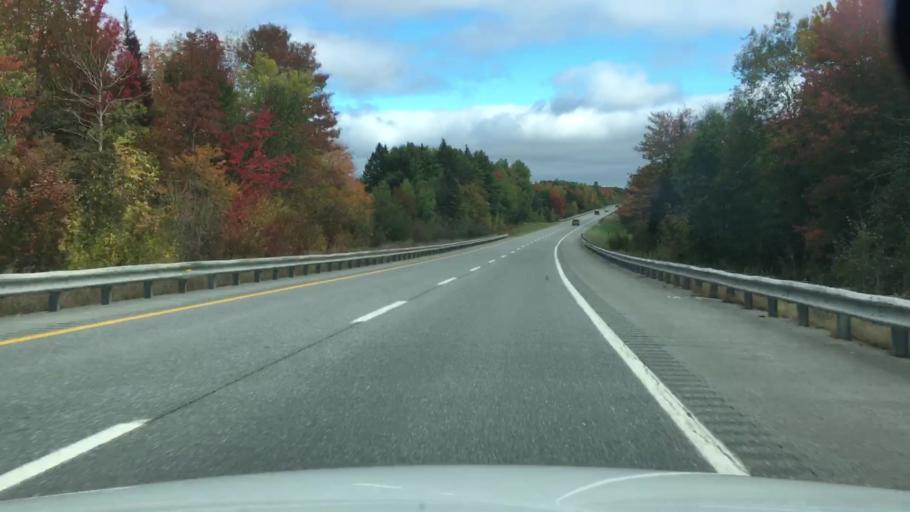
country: US
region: Maine
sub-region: Penobscot County
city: Carmel
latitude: 44.7703
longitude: -69.0023
